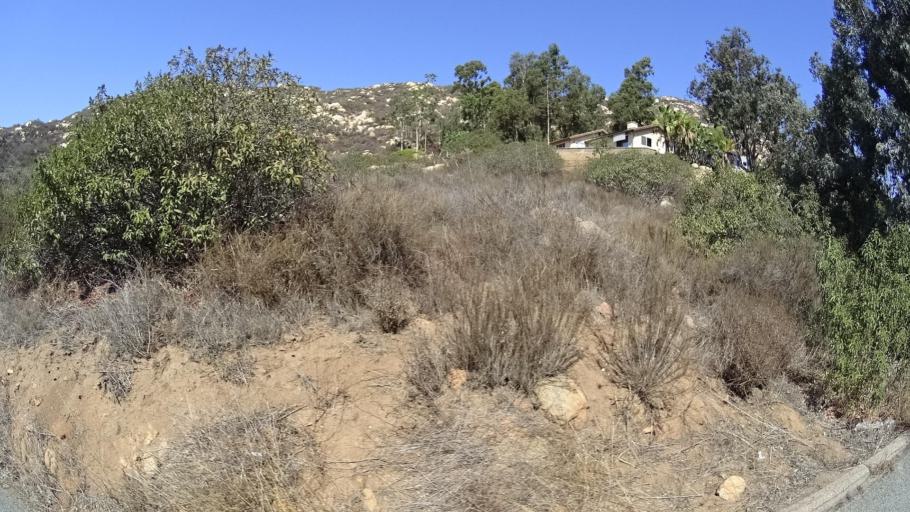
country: US
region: California
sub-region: San Diego County
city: Granite Hills
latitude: 32.8093
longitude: -116.8884
